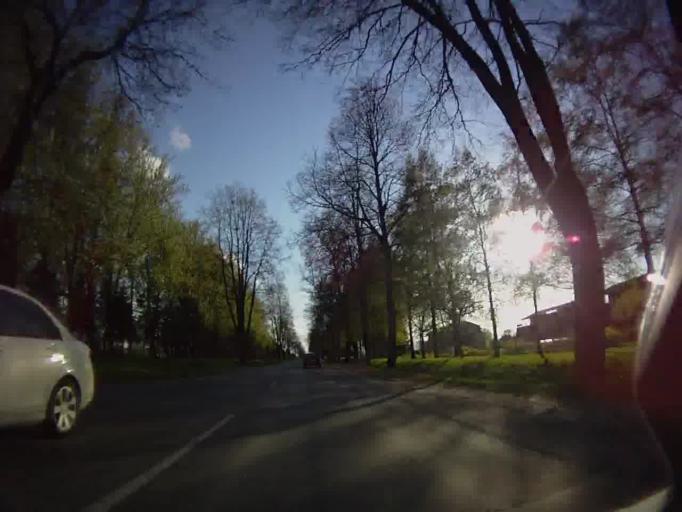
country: LV
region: Sigulda
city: Sigulda
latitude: 57.1509
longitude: 24.8838
